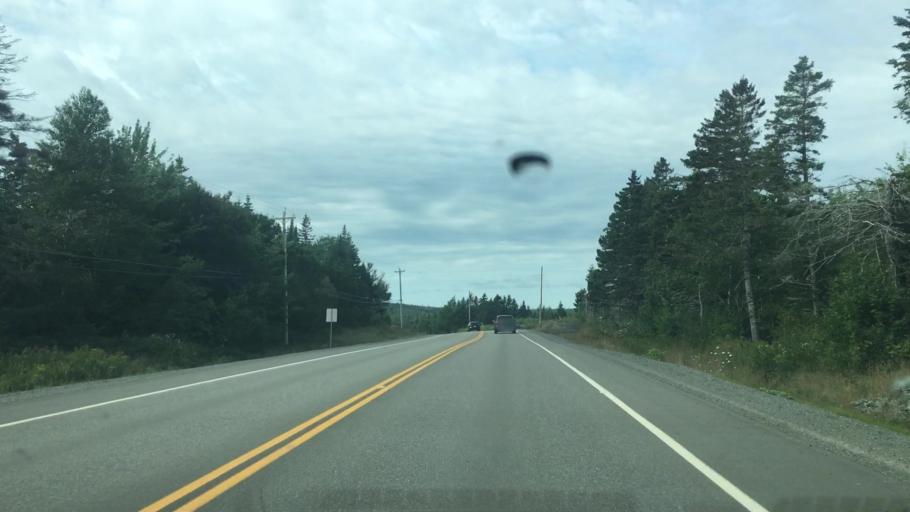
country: CA
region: Nova Scotia
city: Princeville
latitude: 45.6832
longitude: -60.7702
